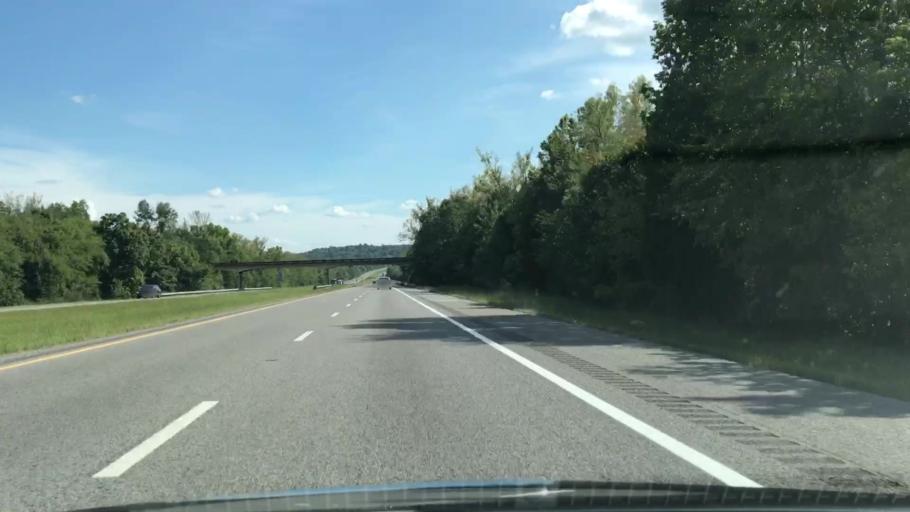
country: US
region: Alabama
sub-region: Limestone County
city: Ardmore
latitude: 35.1401
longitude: -86.8785
